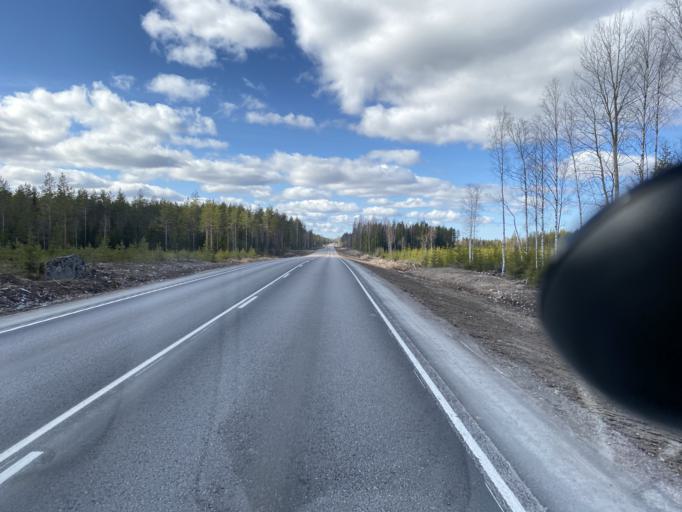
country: FI
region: Satakunta
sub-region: Pori
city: Kokemaeki
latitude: 61.1694
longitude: 22.4609
